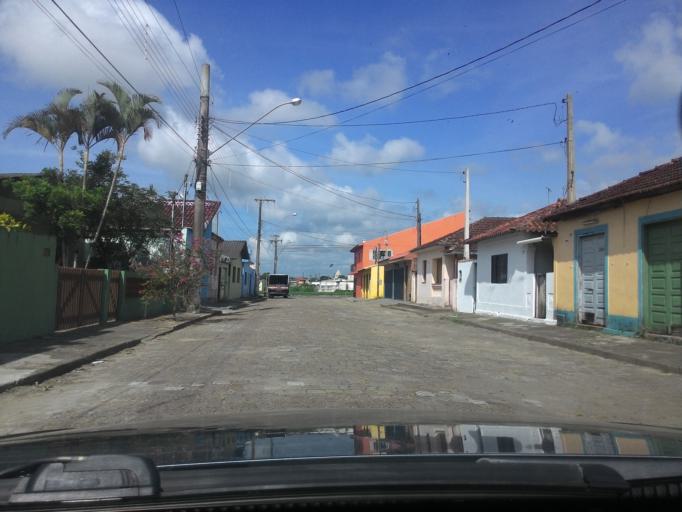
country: BR
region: Sao Paulo
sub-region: Iguape
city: Iguape
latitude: -24.7095
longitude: -47.5618
